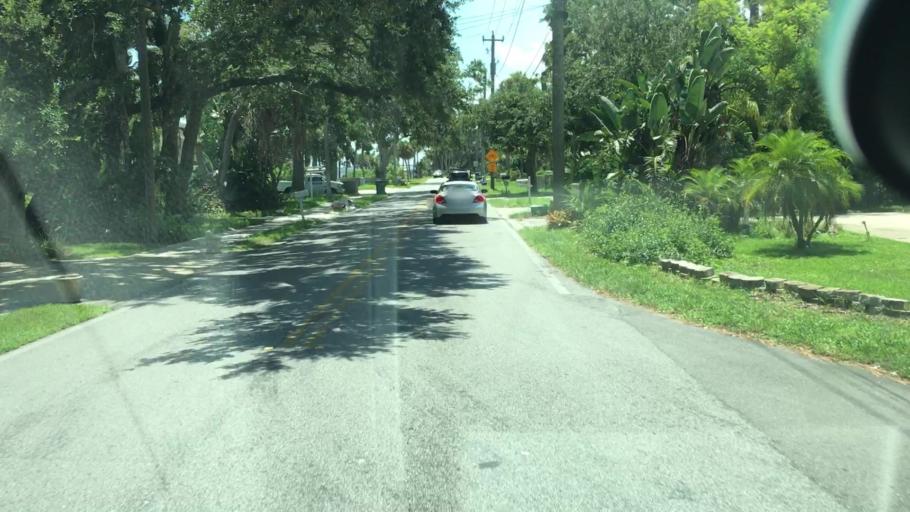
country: US
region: Florida
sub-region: Volusia County
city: Holly Hill
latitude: 29.2578
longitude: -81.0412
